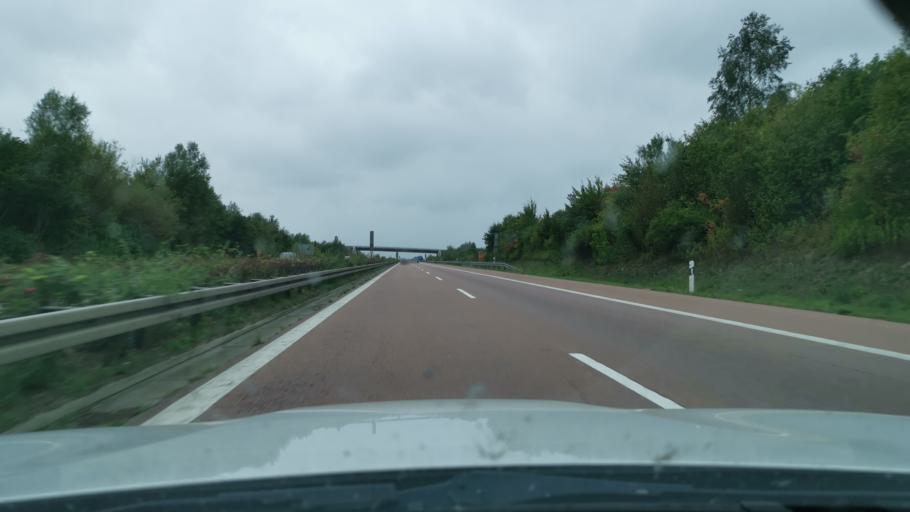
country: DE
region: Mecklenburg-Vorpommern
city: Tessin
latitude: 54.0351
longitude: 12.3899
